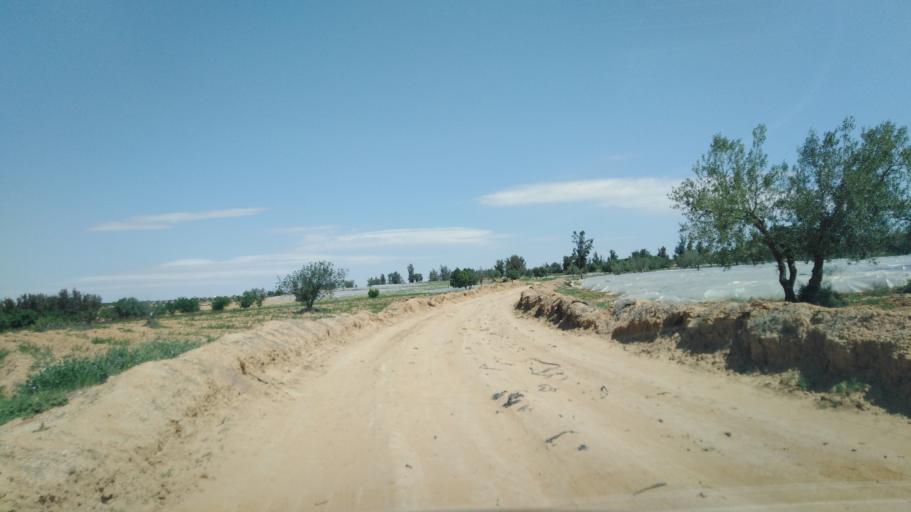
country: TN
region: Safaqis
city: Sfax
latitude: 34.7680
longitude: 10.5274
